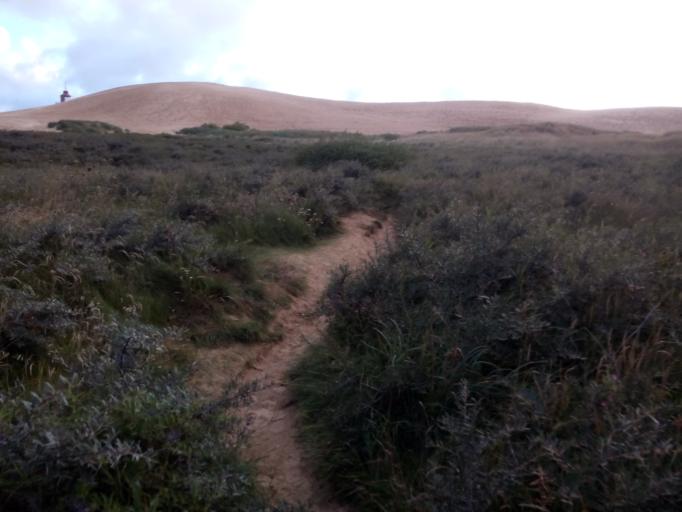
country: DK
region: North Denmark
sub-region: Hjorring Kommune
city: Vra
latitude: 57.4500
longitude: 9.7777
